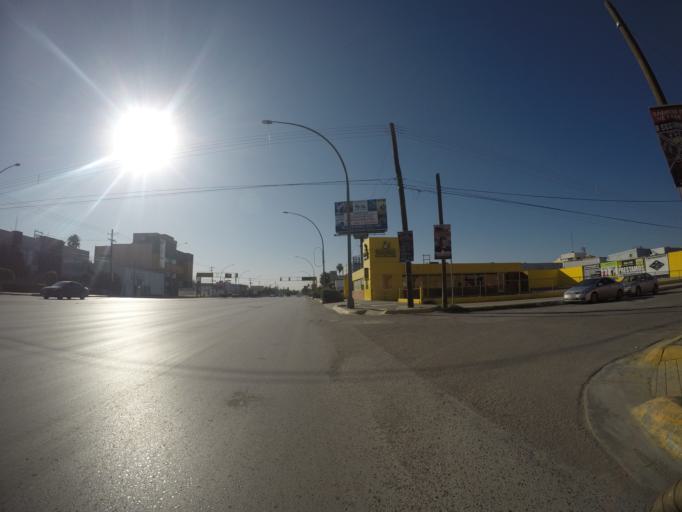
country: MX
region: Chihuahua
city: Ciudad Juarez
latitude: 31.7375
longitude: -106.4547
